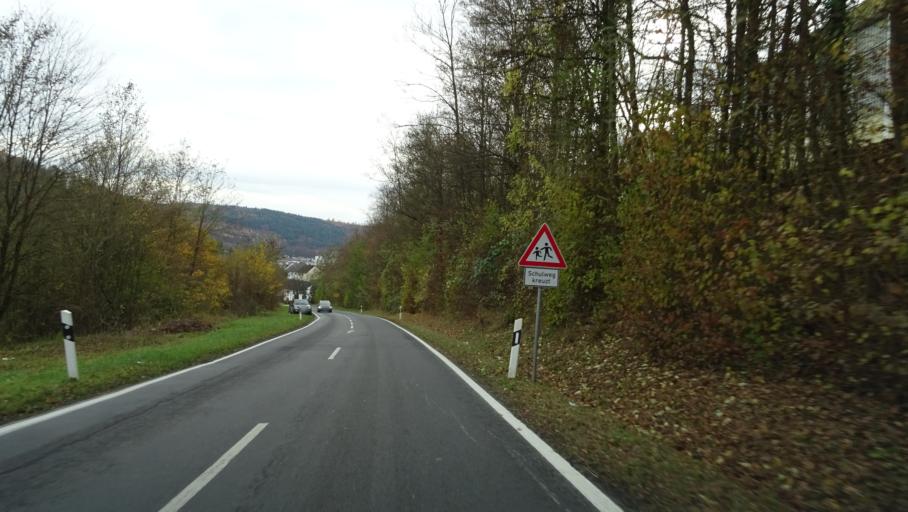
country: DE
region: Baden-Wuerttemberg
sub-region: Karlsruhe Region
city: Mosbach
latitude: 49.3588
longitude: 9.1273
